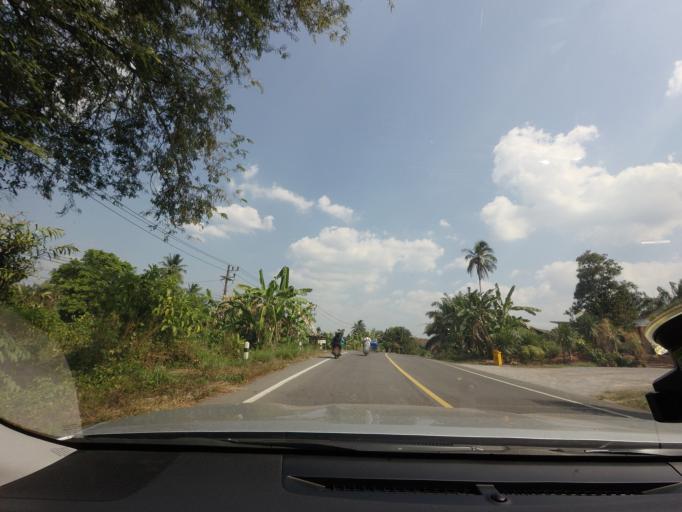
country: TH
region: Phangnga
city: Thap Put
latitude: 8.5308
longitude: 98.6278
